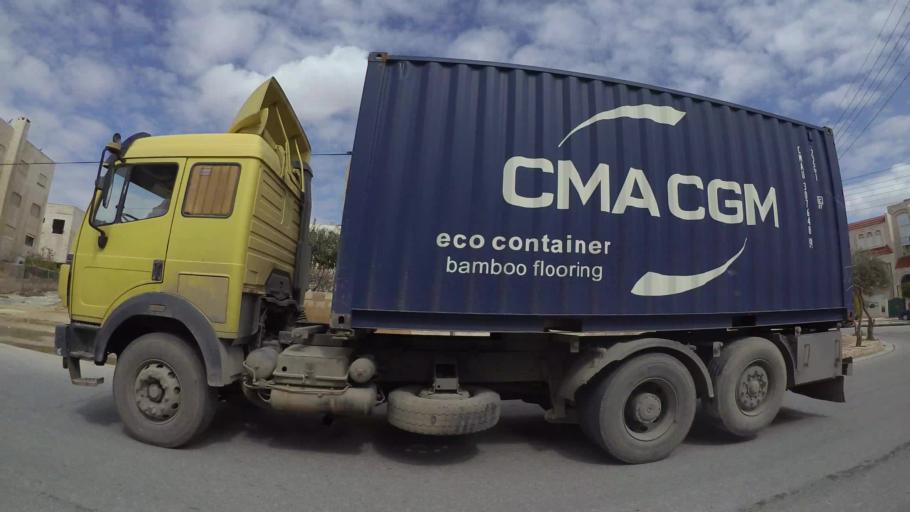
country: JO
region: Amman
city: Amman
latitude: 31.9978
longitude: 35.9140
